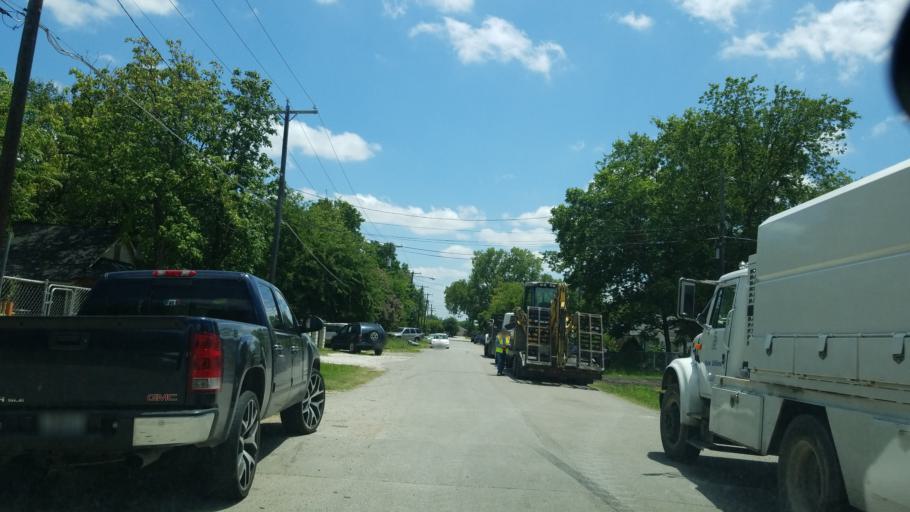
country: US
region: Texas
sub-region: Dallas County
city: Balch Springs
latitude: 32.7331
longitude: -96.7019
